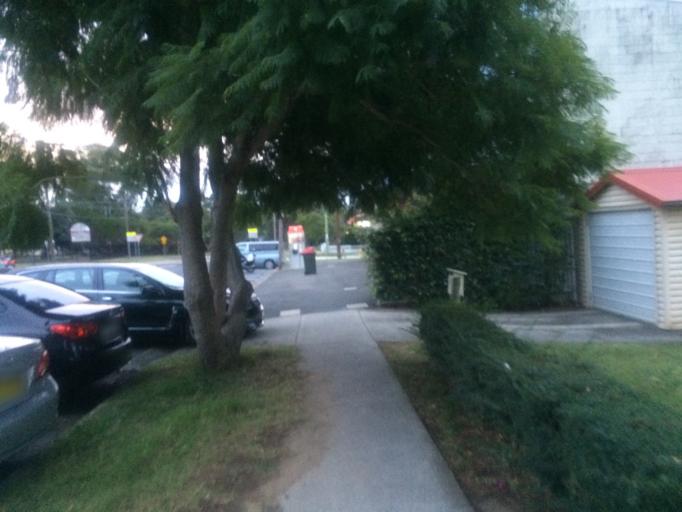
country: AU
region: New South Wales
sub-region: Sutherland Shire
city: Kirrawee
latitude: -34.0283
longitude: 151.0678
